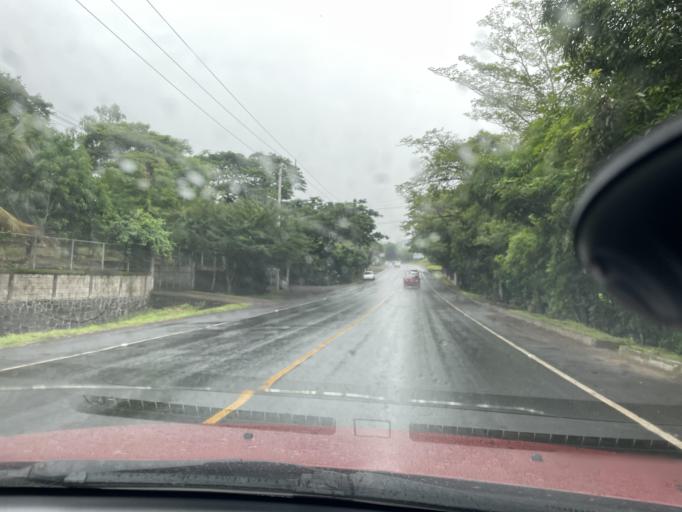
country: SV
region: Morazan
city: Jocoro
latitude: 13.5635
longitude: -88.0983
